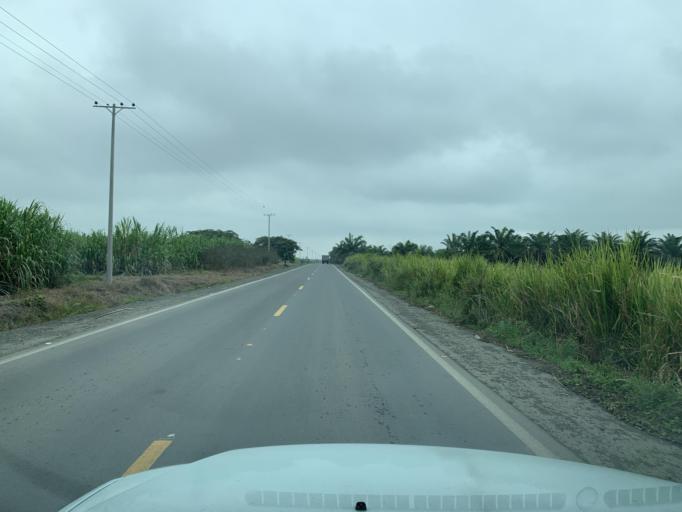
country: EC
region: Guayas
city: Coronel Marcelino Mariduena
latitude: -2.3214
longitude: -79.5189
